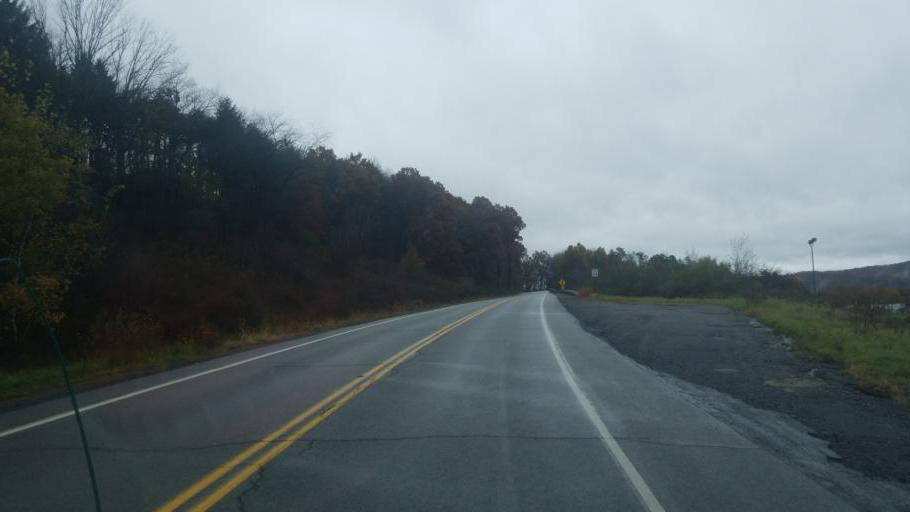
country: US
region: Pennsylvania
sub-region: Clearfield County
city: Clearfield
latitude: 41.0433
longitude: -78.3934
